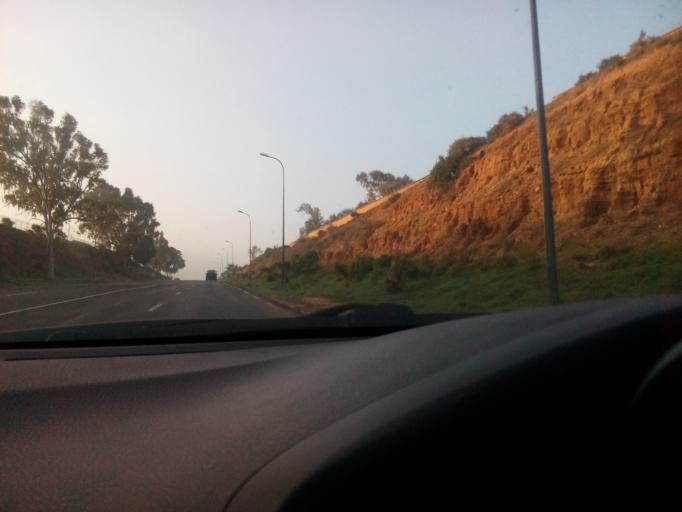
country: DZ
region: Oran
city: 'Ain el Turk
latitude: 35.7175
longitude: -0.8529
